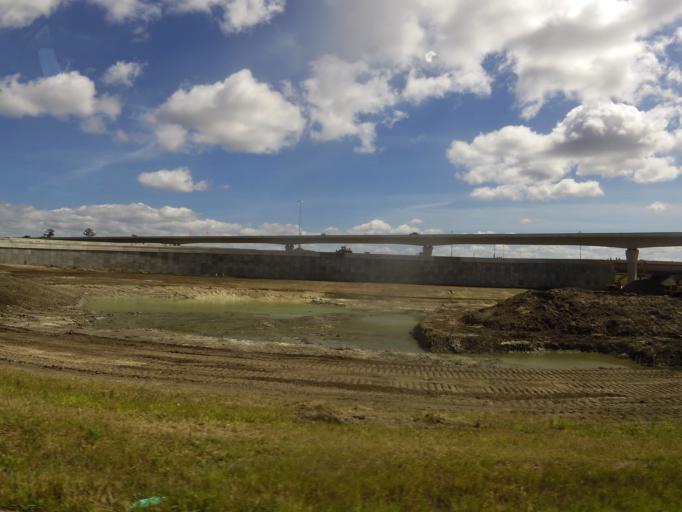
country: US
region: Florida
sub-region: Duval County
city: Jacksonville
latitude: 30.4620
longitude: -81.6476
